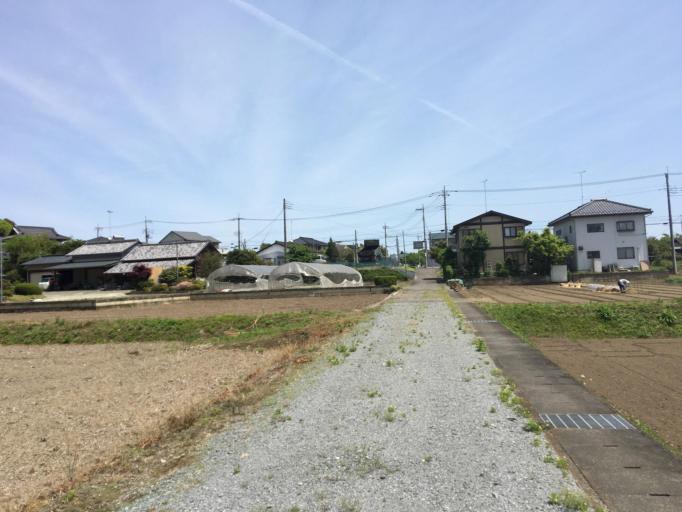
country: JP
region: Tochigi
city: Mibu
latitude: 36.4434
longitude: 139.7965
